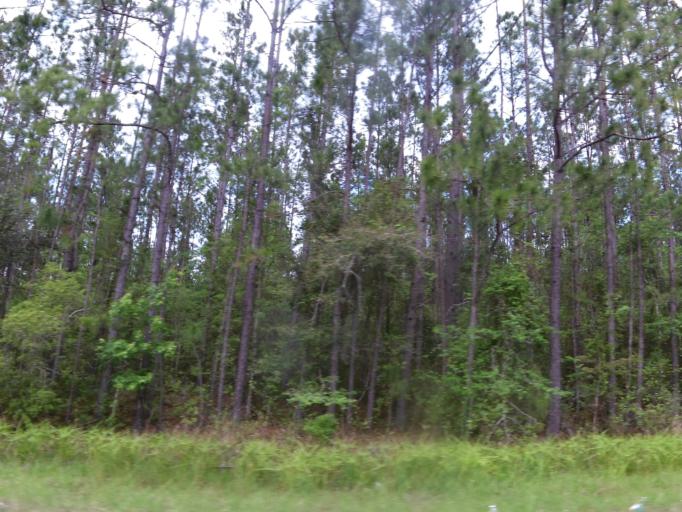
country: US
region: Georgia
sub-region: Charlton County
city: Folkston
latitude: 30.8291
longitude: -81.8727
